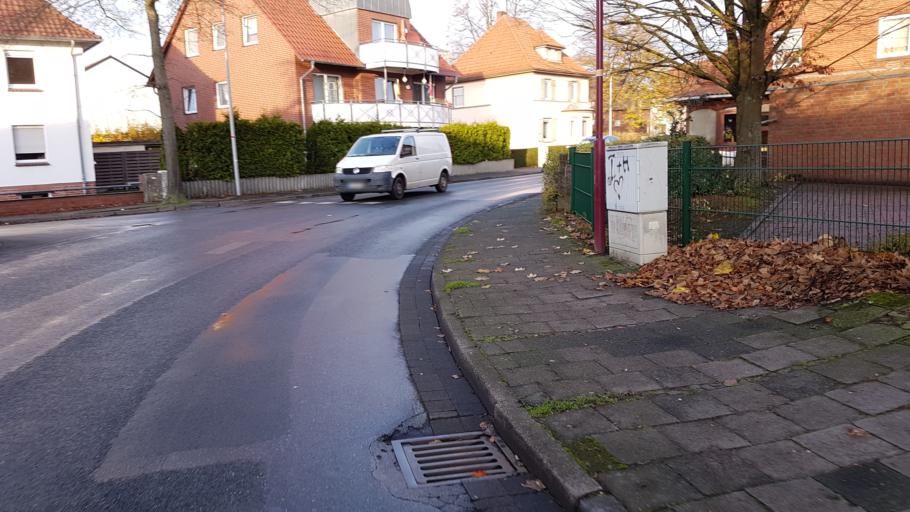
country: DE
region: North Rhine-Westphalia
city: Rahden
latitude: 52.4344
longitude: 8.6177
